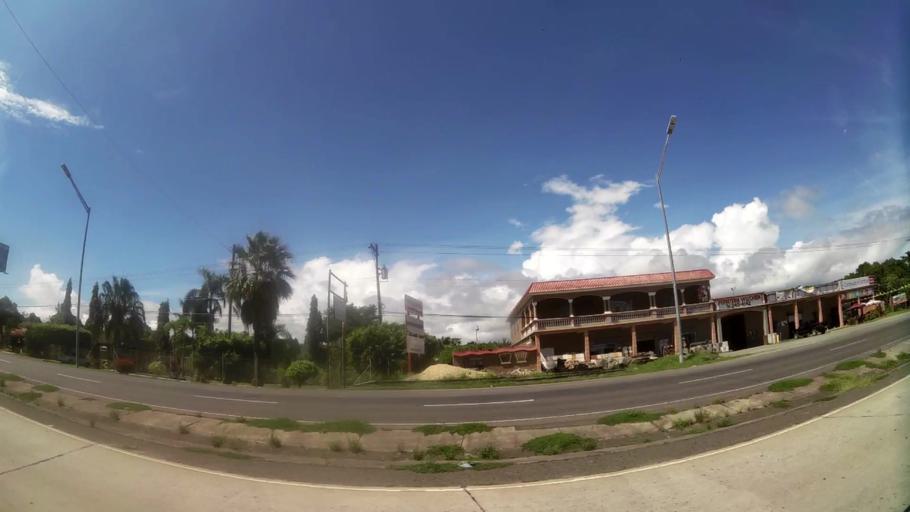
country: PA
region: Panama
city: Chame
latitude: 8.5582
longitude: -79.9039
